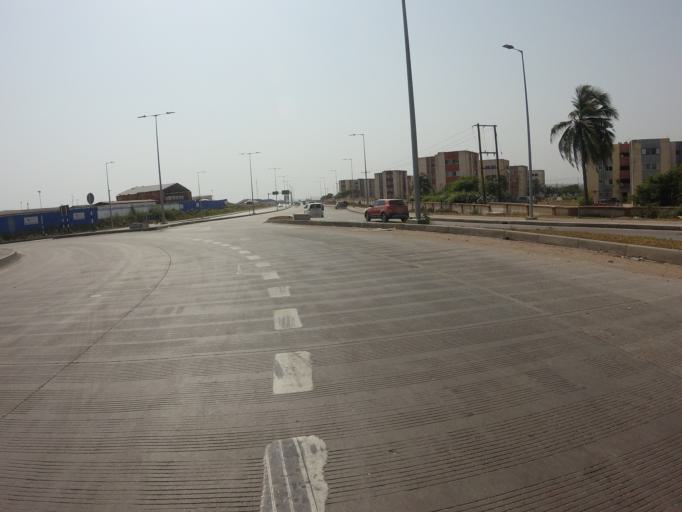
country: GH
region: Greater Accra
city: Tema
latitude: 5.6171
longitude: -0.0231
